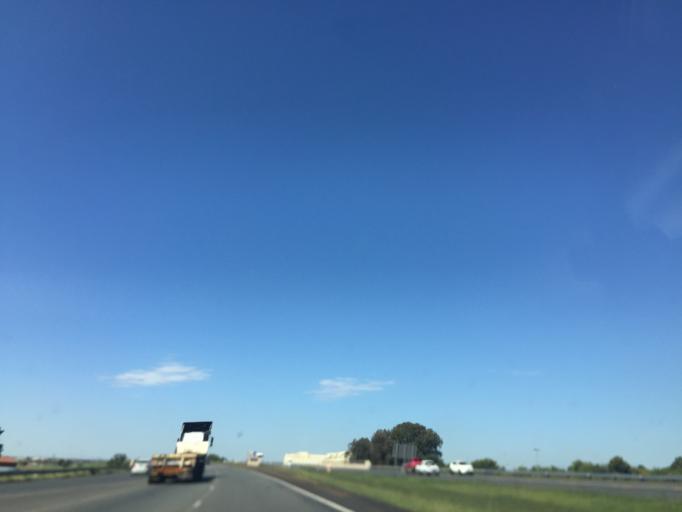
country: ZA
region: Gauteng
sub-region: Sedibeng District Municipality
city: Vereeniging
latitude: -26.6558
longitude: 27.9194
